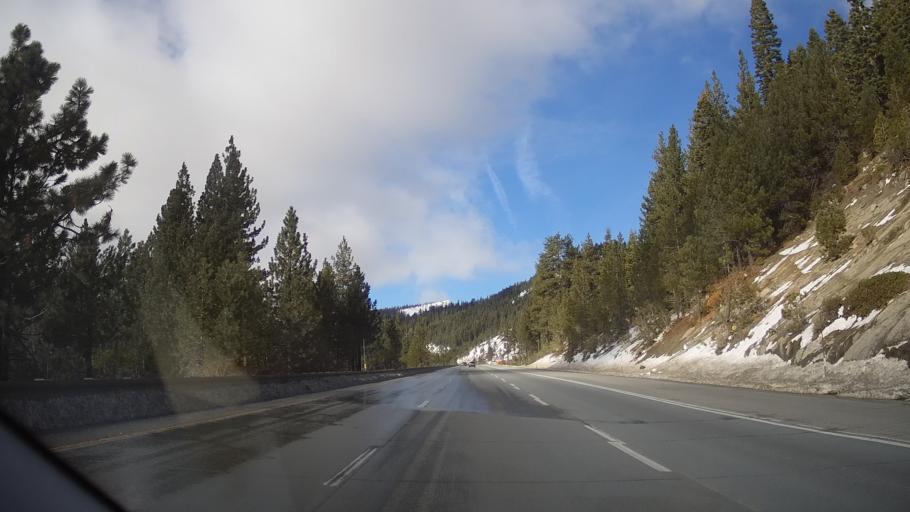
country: US
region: California
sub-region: Nevada County
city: Truckee
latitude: 39.3302
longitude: -120.3023
